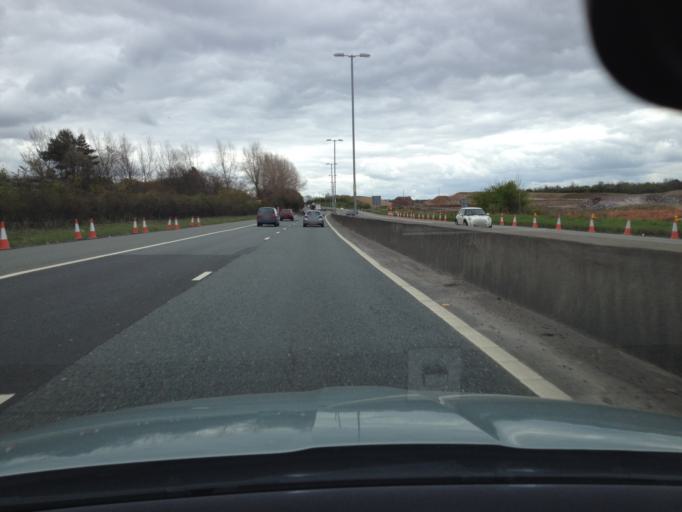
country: GB
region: Scotland
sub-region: South Lanarkshire
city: Uddingston
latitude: 55.8460
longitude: -4.0596
